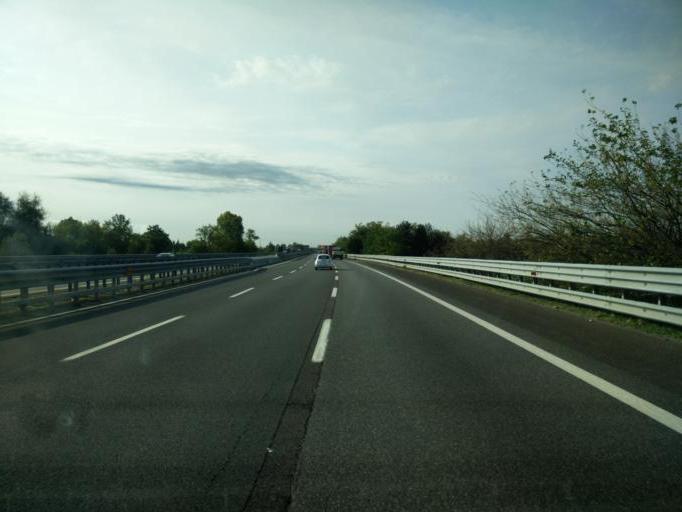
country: IT
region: Lombardy
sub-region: Provincia di Brescia
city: San Zeno Naviglio
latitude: 45.4937
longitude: 10.2282
